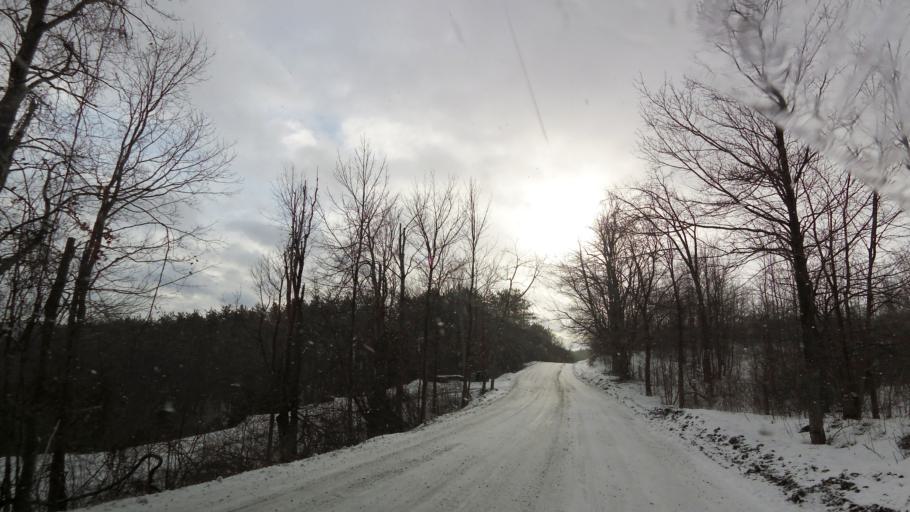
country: CA
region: Ontario
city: Orangeville
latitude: 43.8362
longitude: -79.9737
